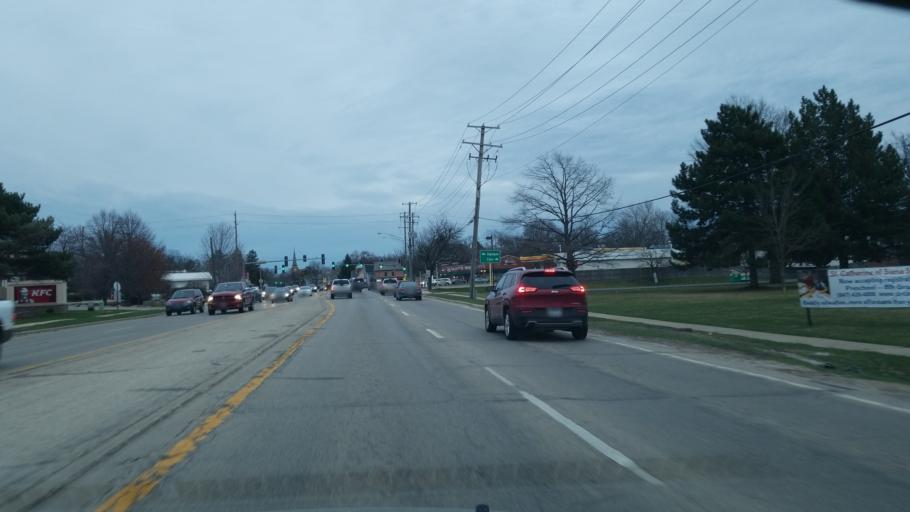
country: US
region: Illinois
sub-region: Kane County
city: West Dundee
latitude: 42.0983
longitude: -88.2891
